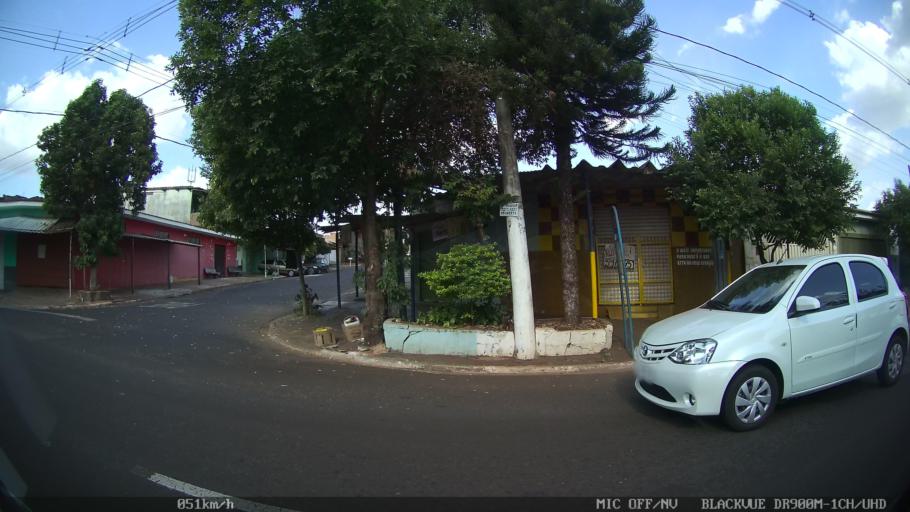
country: BR
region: Sao Paulo
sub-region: Ribeirao Preto
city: Ribeirao Preto
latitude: -21.1948
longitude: -47.8488
